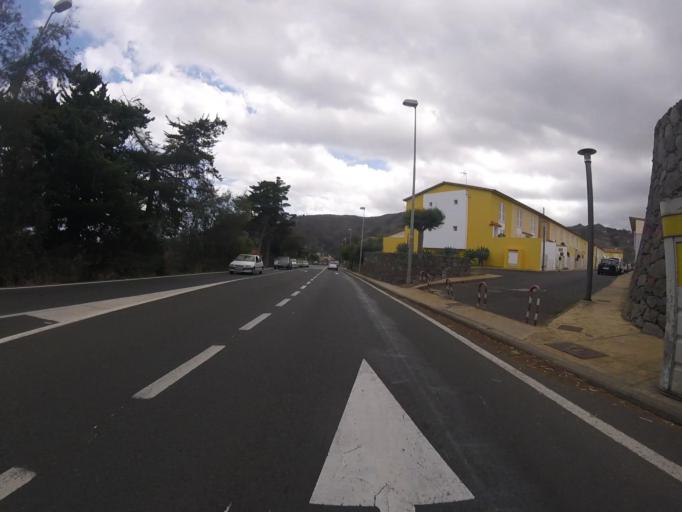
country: ES
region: Canary Islands
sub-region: Provincia de Las Palmas
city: Santa Brigida
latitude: 28.0278
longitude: -15.5070
